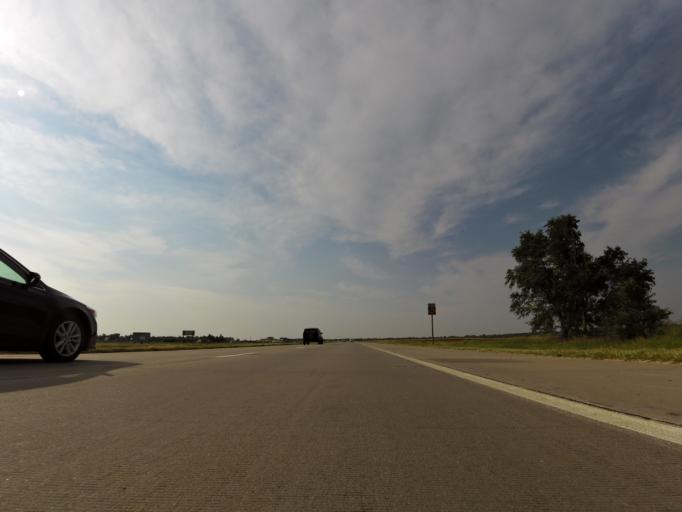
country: US
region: Kansas
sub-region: Sedgwick County
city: Colwich
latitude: 37.8694
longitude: -97.6240
